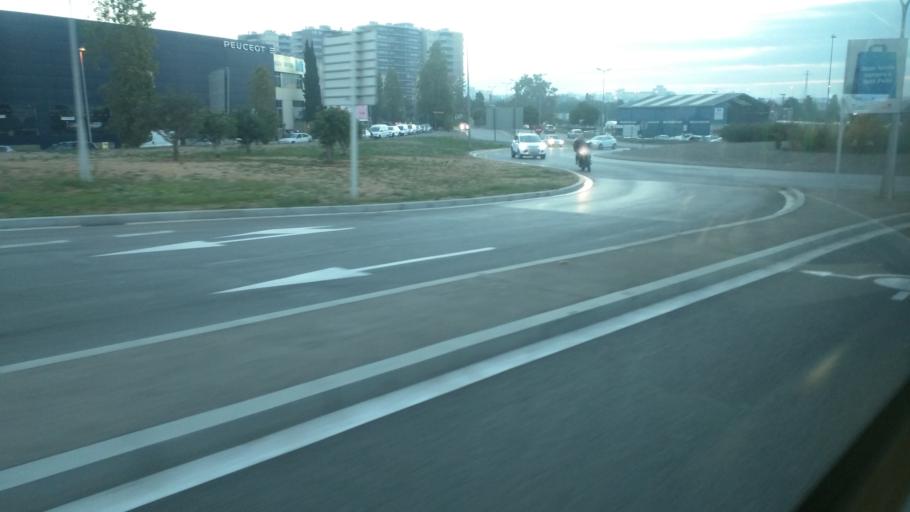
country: ES
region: Catalonia
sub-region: Provincia de Barcelona
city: Sant Feliu de Llobregat
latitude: 41.3748
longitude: 2.0425
